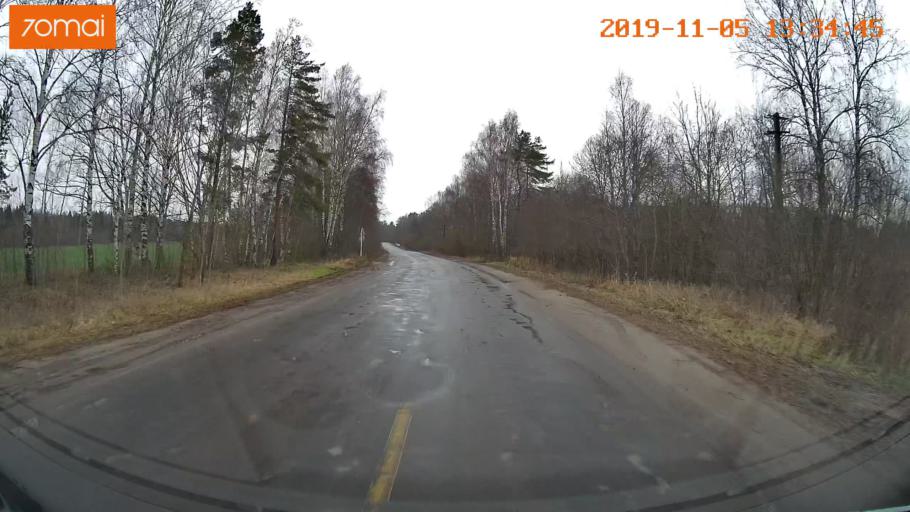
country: RU
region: Ivanovo
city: Shuya
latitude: 56.9031
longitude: 41.3898
